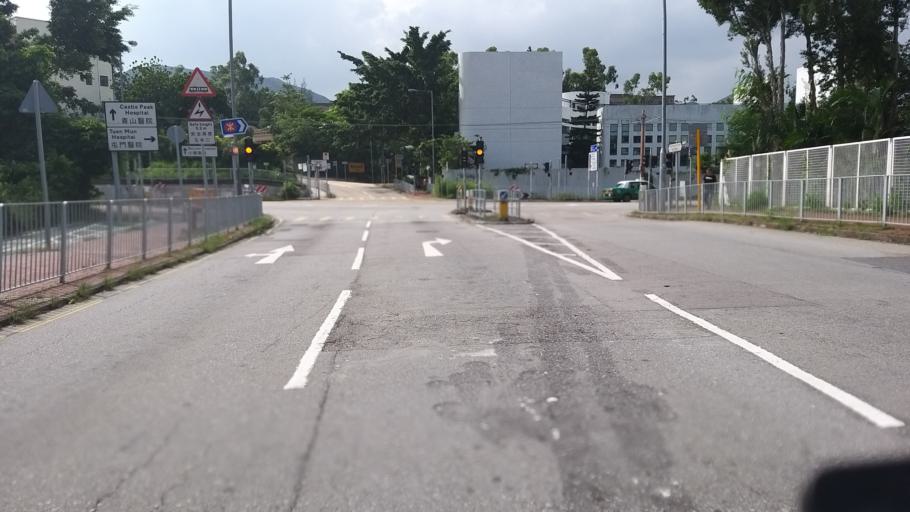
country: HK
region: Tuen Mun
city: Tuen Mun
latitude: 22.4075
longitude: 113.9746
